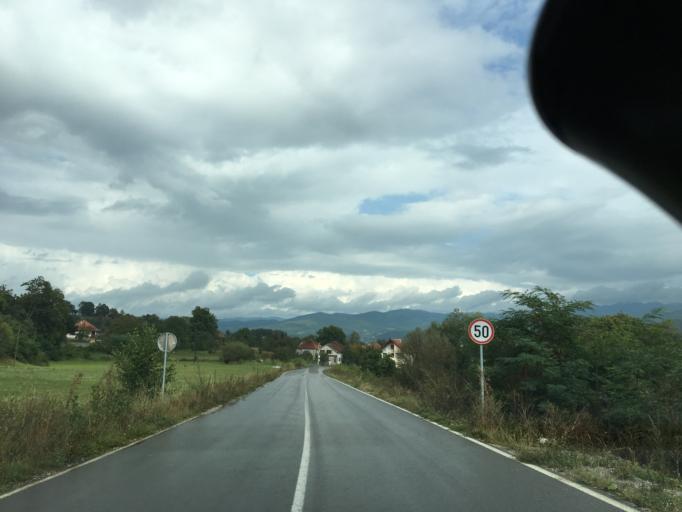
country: ME
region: Berane
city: Berane
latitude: 42.8274
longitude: 19.8390
